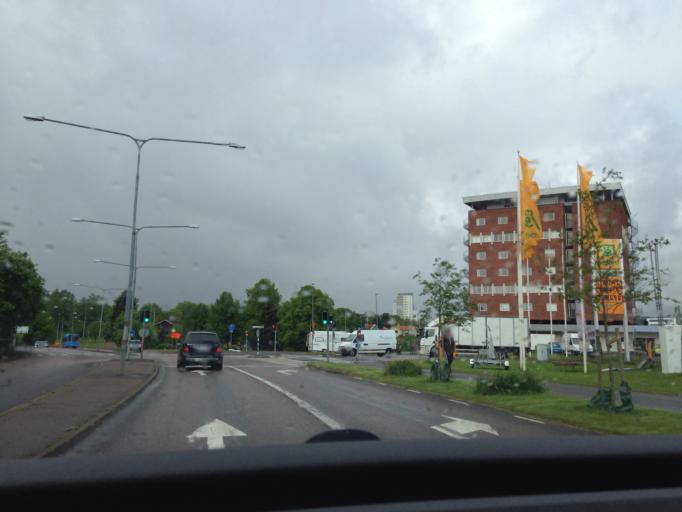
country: SE
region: Vaestra Goetaland
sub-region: Skovde Kommun
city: Skoevde
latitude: 58.3930
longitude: 13.8675
